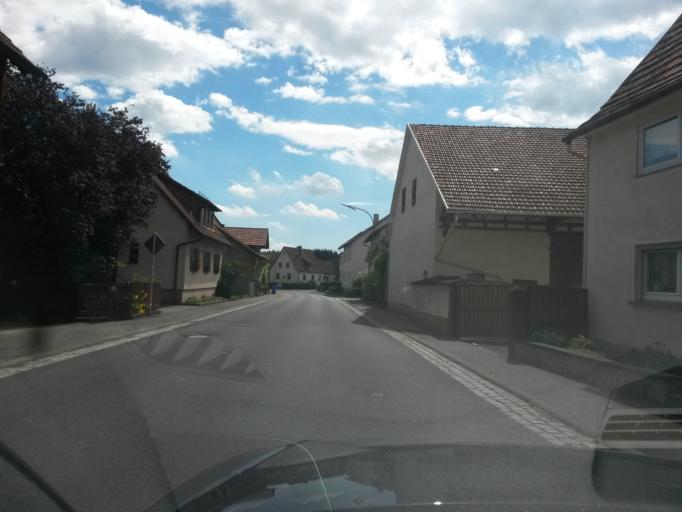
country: DE
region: Bavaria
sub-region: Regierungsbezirk Unterfranken
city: Fladungen
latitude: 50.5282
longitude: 10.1399
